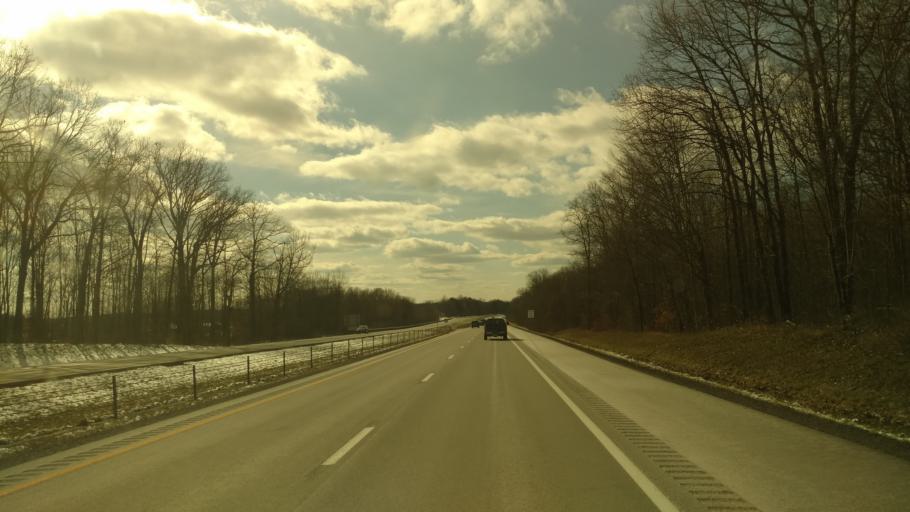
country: US
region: Ohio
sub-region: Portage County
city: Ravenna
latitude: 41.1058
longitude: -81.1700
